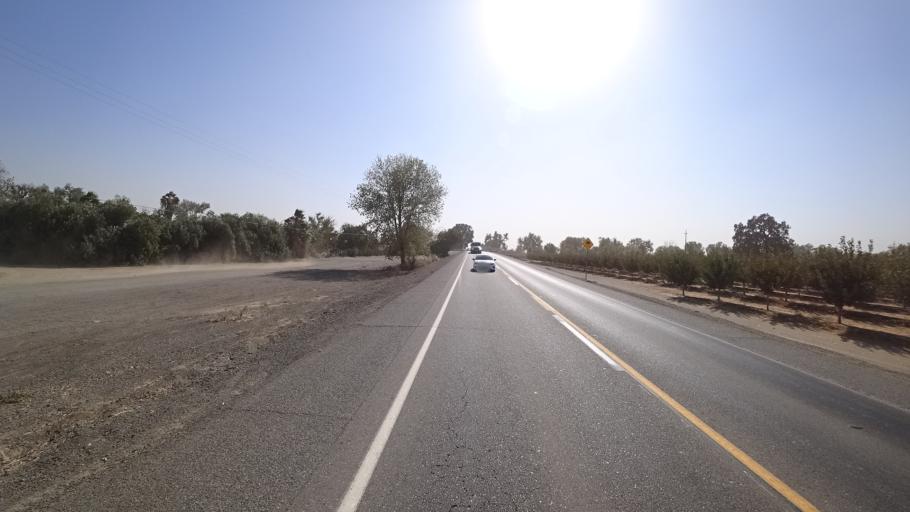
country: US
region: California
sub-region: Yolo County
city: Woodland
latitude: 38.7290
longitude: -121.7298
